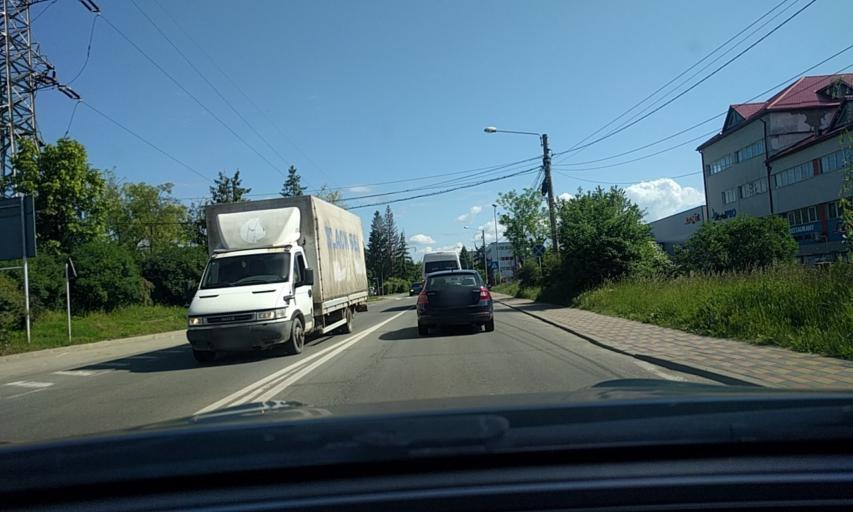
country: RO
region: Bistrita-Nasaud
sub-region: Municipiul Bistrita
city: Viisoara
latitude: 47.1289
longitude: 24.4683
